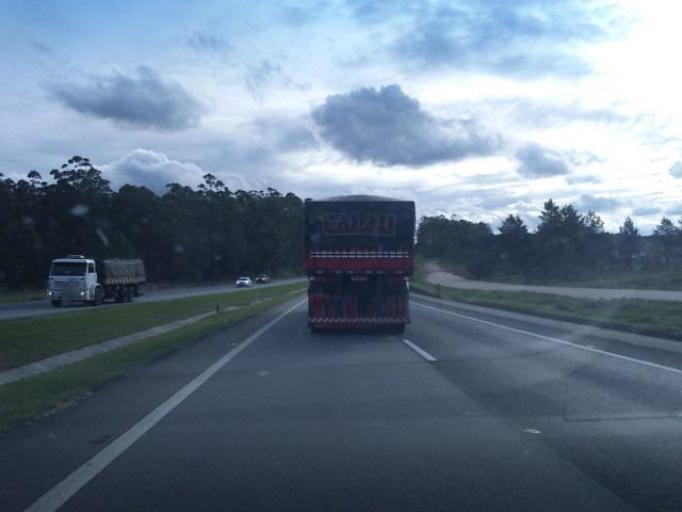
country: BR
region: Parana
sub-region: Piraquara
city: Piraquara
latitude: -25.4247
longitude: -49.0756
